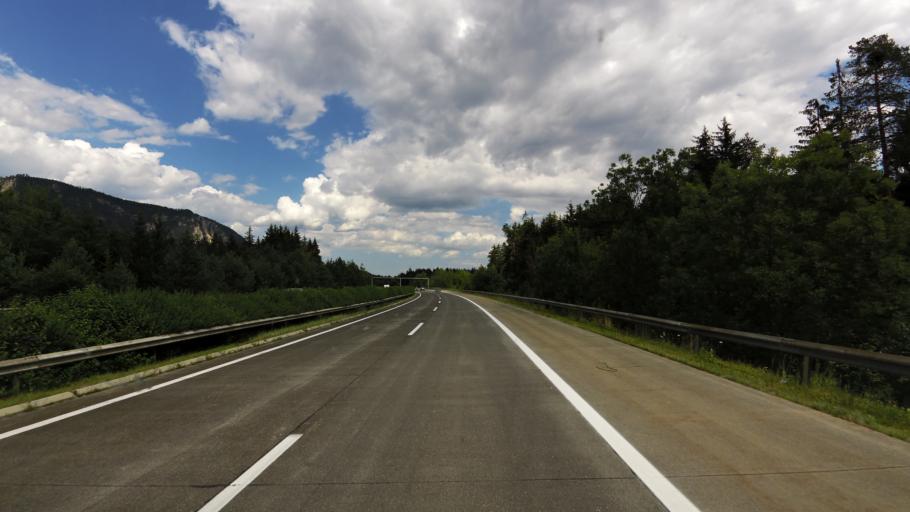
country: AT
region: Carinthia
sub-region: Politischer Bezirk Villach Land
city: Arnoldstein
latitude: 46.5576
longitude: 13.7563
